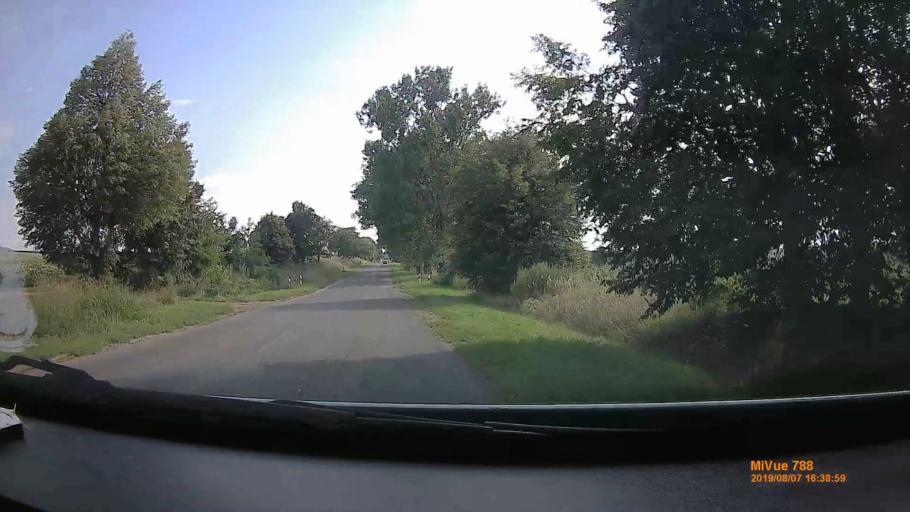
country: HU
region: Borsod-Abauj-Zemplen
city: Gonc
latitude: 48.3972
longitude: 21.2248
